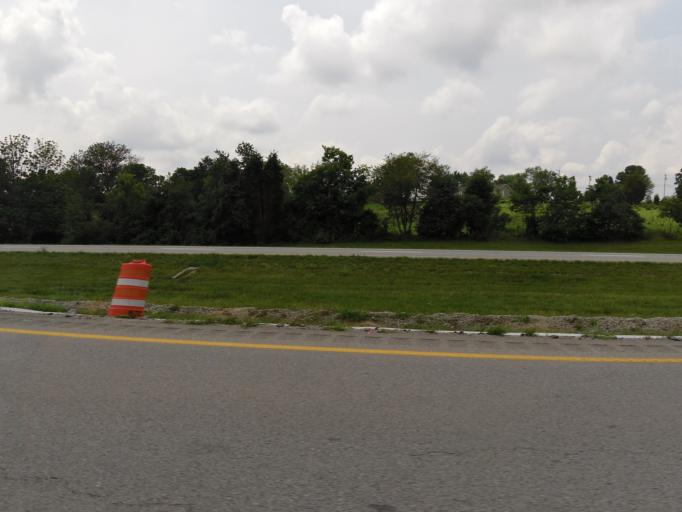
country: US
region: Kentucky
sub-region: Oldham County
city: La Grange
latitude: 38.4467
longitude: -85.3055
